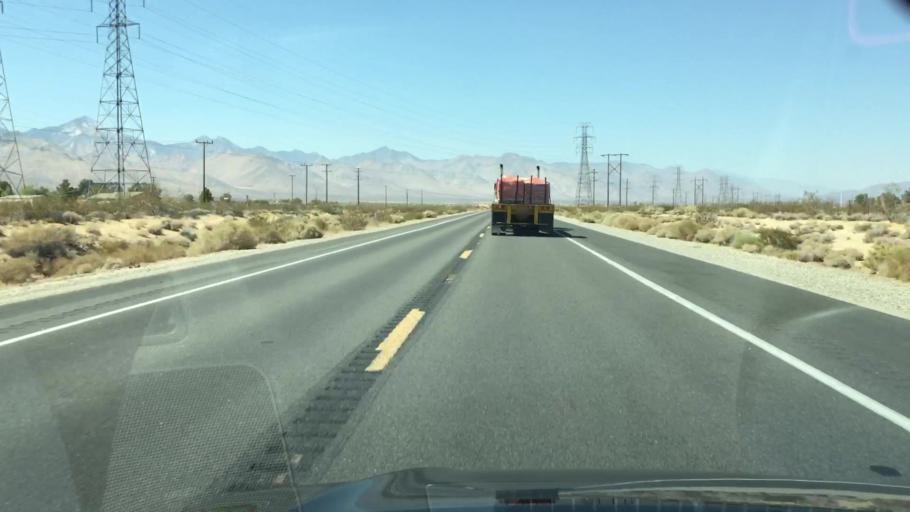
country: US
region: California
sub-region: Kern County
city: Inyokern
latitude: 35.6395
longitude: -117.7903
